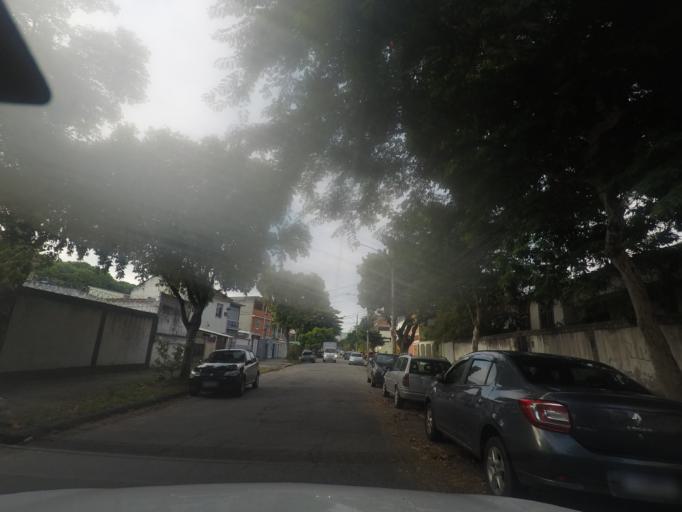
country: BR
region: Rio de Janeiro
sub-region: Duque De Caxias
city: Duque de Caxias
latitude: -22.8318
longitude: -43.2723
